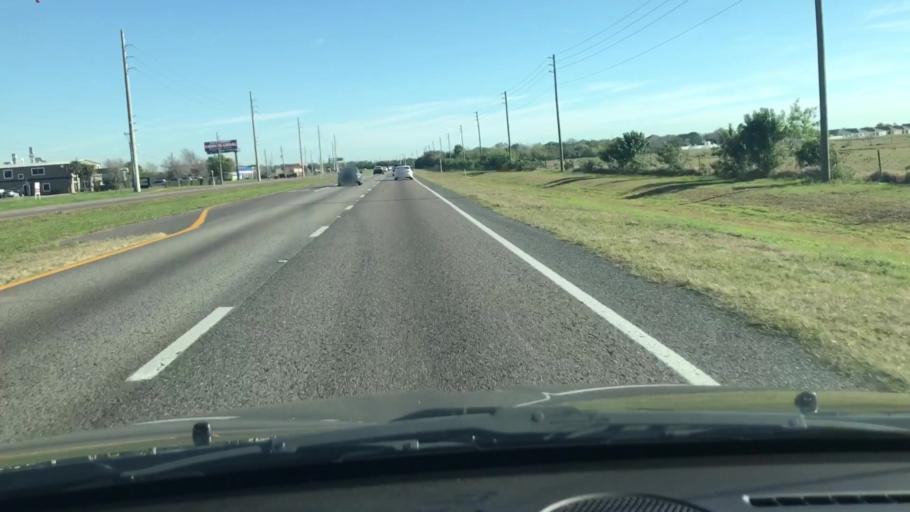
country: US
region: Florida
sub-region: Osceola County
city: Kissimmee
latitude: 28.2725
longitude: -81.4225
